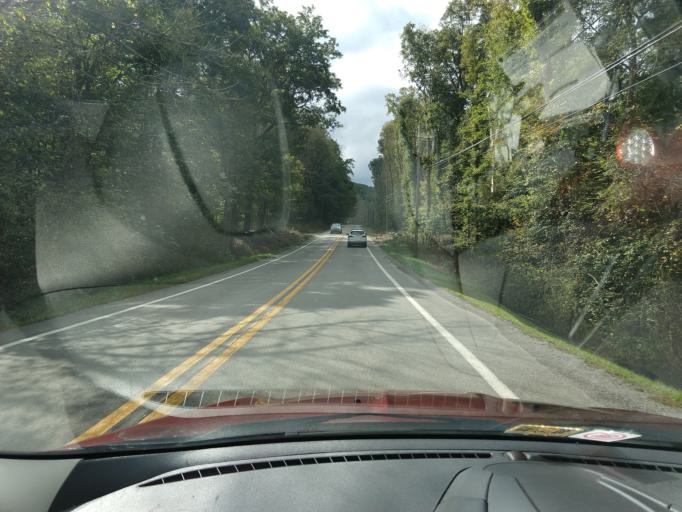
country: US
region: West Virginia
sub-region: Barbour County
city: Belington
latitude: 38.9882
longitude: -79.9385
